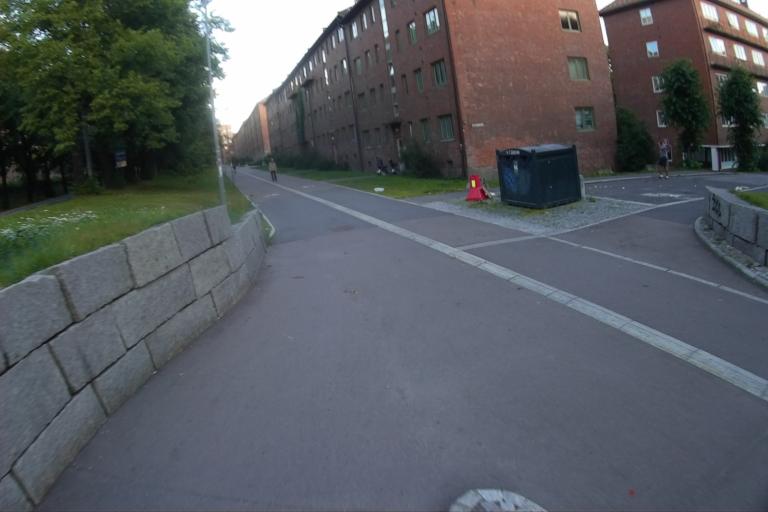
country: NO
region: Oslo
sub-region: Oslo
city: Oslo
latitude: 59.9290
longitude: 10.7698
